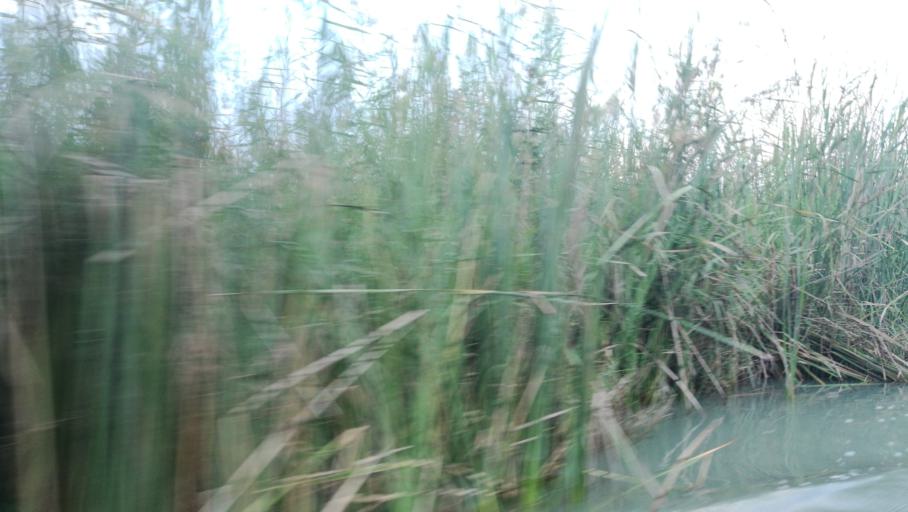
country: IQ
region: Dhi Qar
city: Al Jabayish
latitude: 30.9841
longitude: 47.0432
